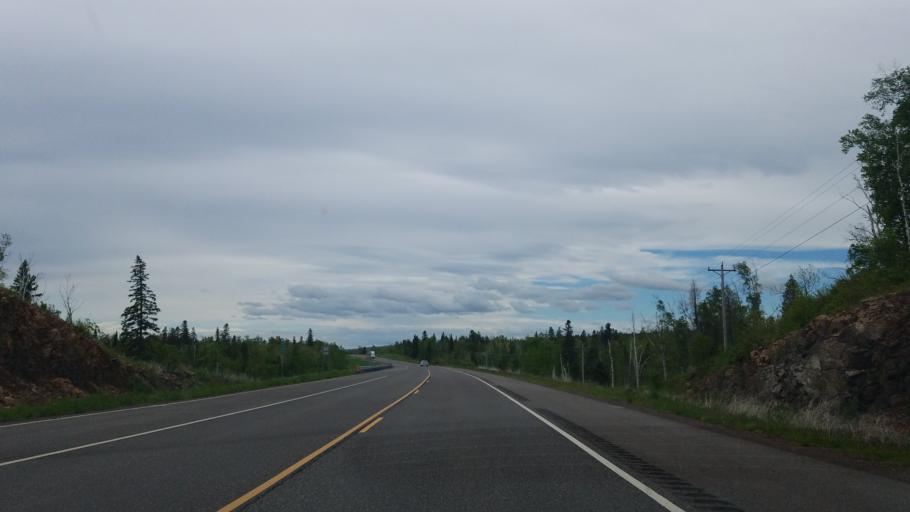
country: US
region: Minnesota
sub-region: Lake County
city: Silver Bay
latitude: 47.1988
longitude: -91.3820
